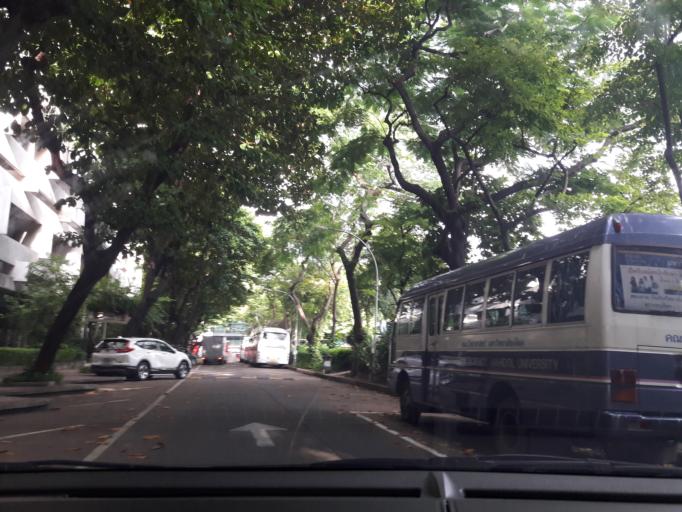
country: TH
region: Bangkok
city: Ratchathewi
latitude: 13.7644
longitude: 100.5251
